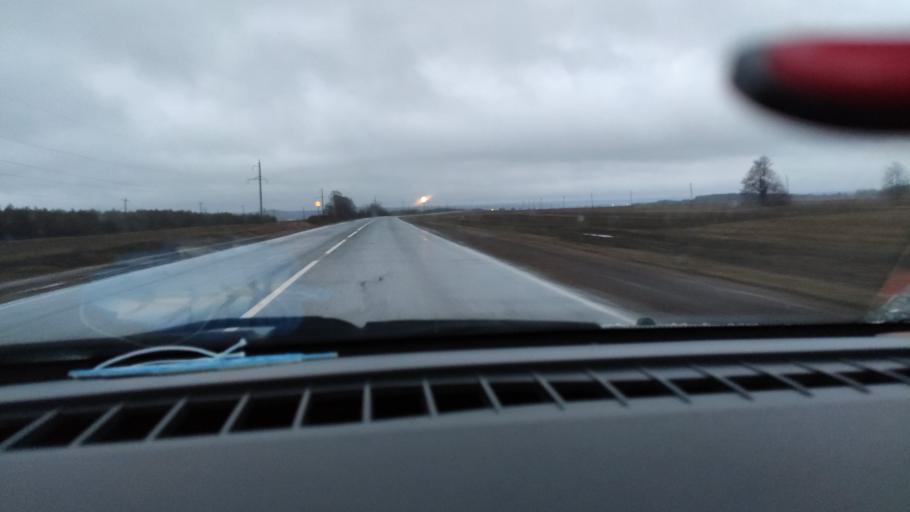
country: RU
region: Udmurtiya
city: Alnashi
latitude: 56.2024
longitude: 52.4497
